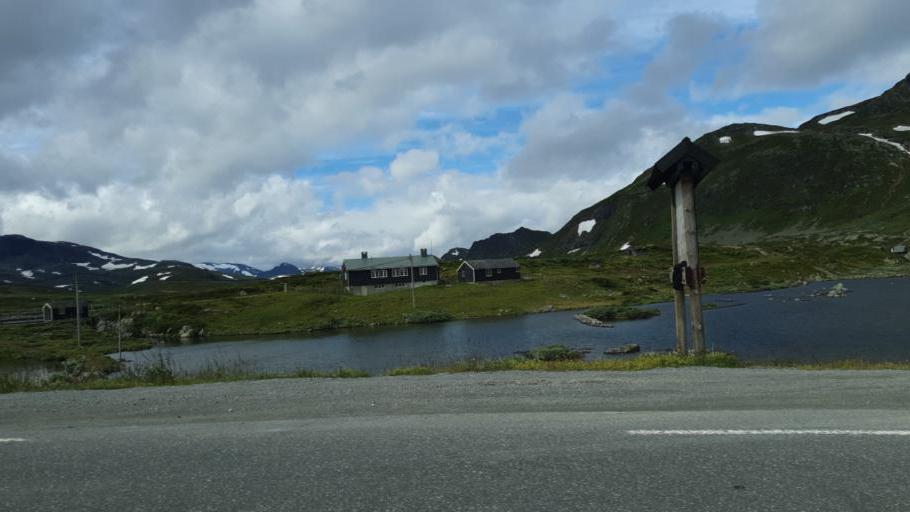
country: NO
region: Oppland
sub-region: Vestre Slidre
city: Slidre
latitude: 61.3291
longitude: 8.7991
